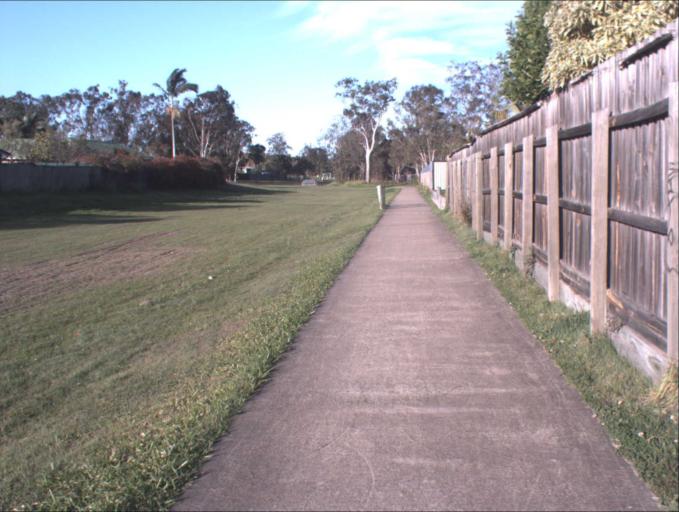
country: AU
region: Queensland
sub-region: Logan
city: Logan Reserve
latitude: -27.6922
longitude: 153.0861
